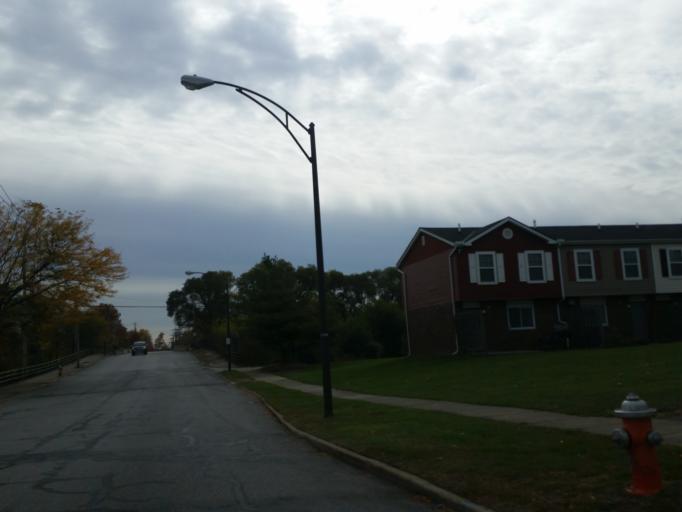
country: US
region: Ohio
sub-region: Cuyahoga County
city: Newburgh Heights
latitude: 41.4870
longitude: -81.6365
